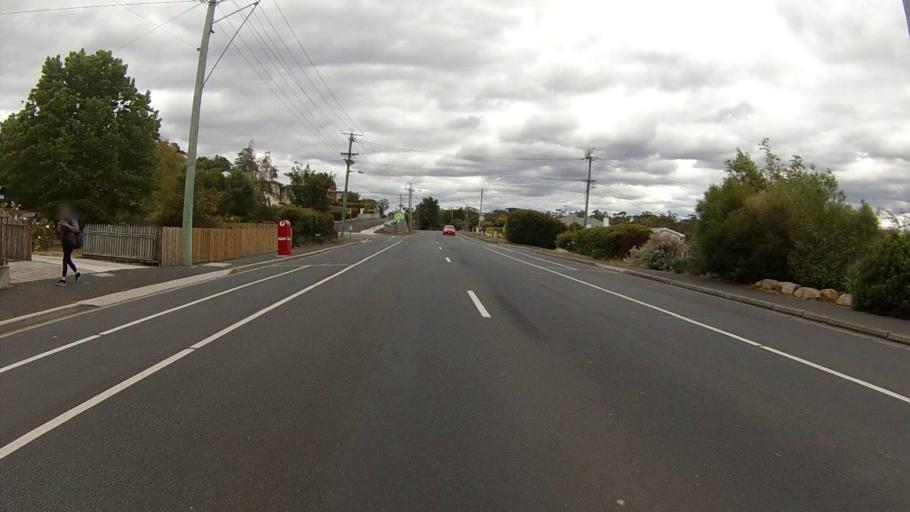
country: AU
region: Tasmania
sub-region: Glenorchy
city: Claremont
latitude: -42.7799
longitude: 147.2521
